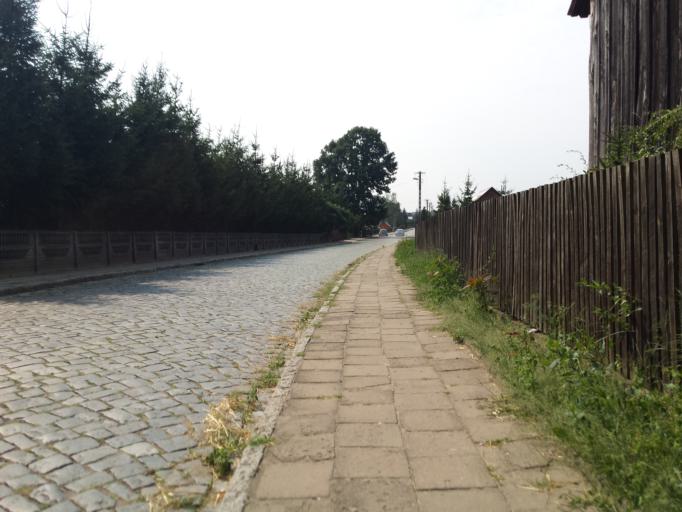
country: PL
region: Greater Poland Voivodeship
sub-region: Powiat czarnkowsko-trzcianecki
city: Polajewo
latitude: 52.7728
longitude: 16.6414
